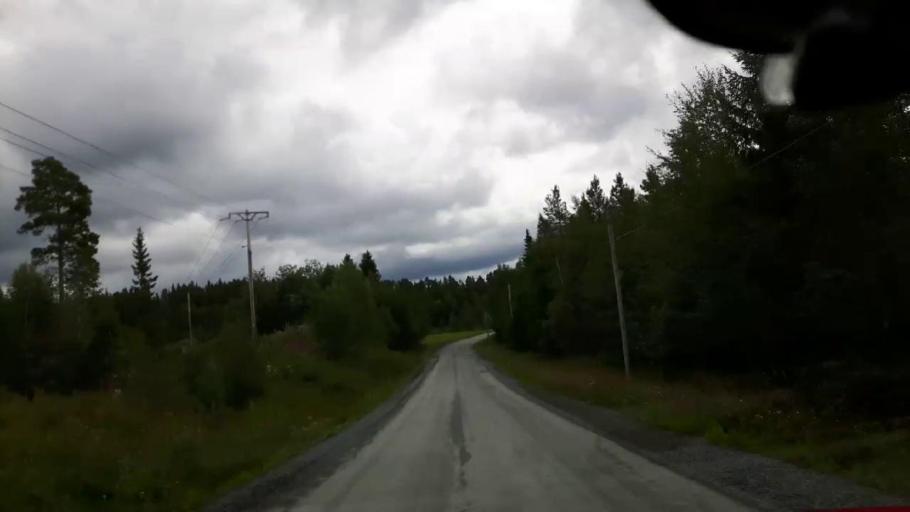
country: SE
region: Jaemtland
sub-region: Krokoms Kommun
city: Krokom
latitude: 63.5738
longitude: 14.2386
